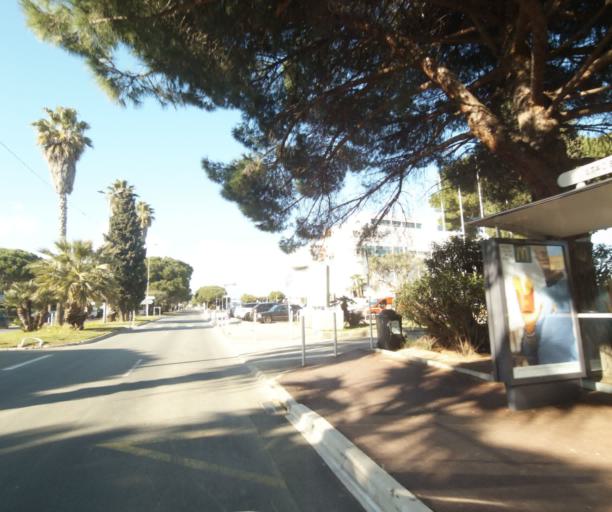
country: FR
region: Provence-Alpes-Cote d'Azur
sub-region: Departement des Alpes-Maritimes
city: Antibes
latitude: 43.5892
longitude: 7.1180
